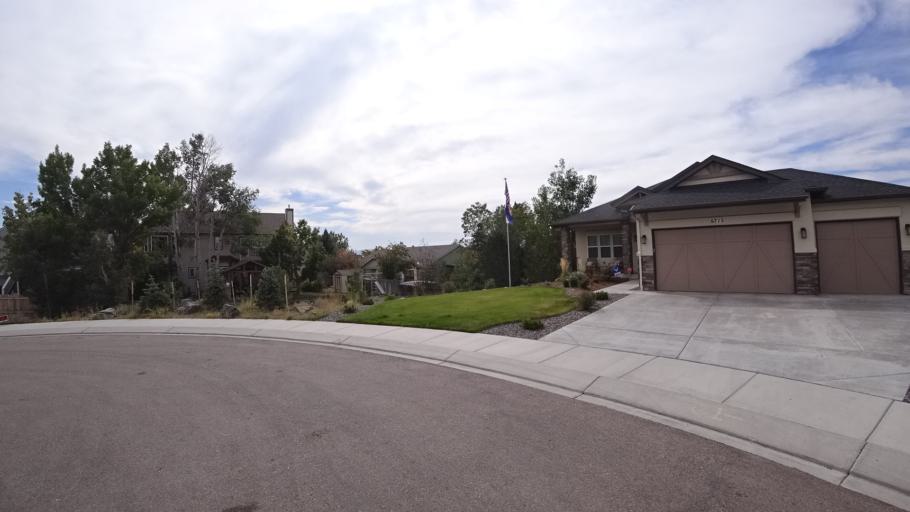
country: US
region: Colorado
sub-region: El Paso County
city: Cimarron Hills
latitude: 38.9035
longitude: -104.7025
